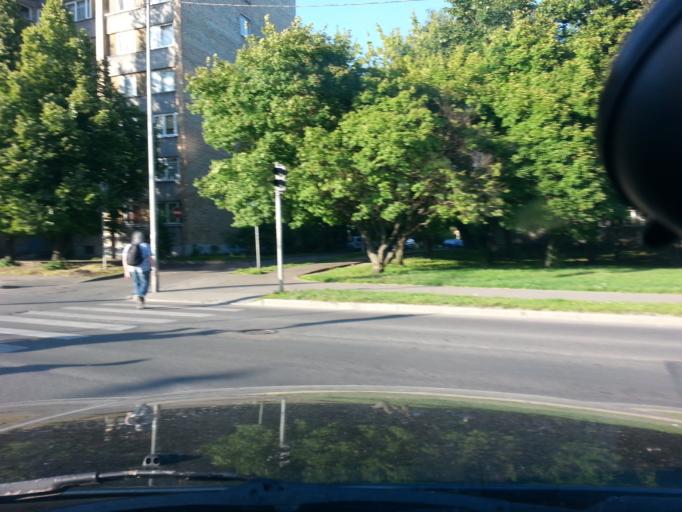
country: LV
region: Kekava
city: Balozi
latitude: 56.9180
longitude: 24.1737
